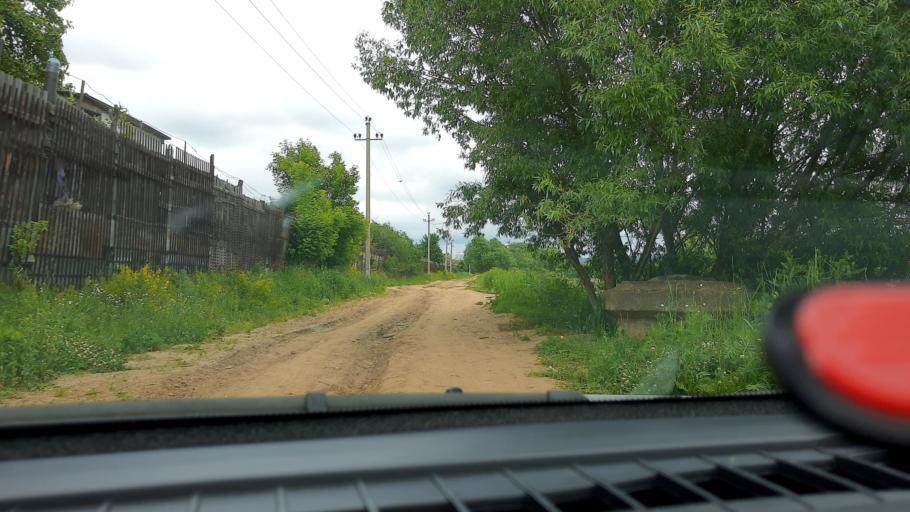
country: RU
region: Nizjnij Novgorod
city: Burevestnik
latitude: 56.2107
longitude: 43.8361
